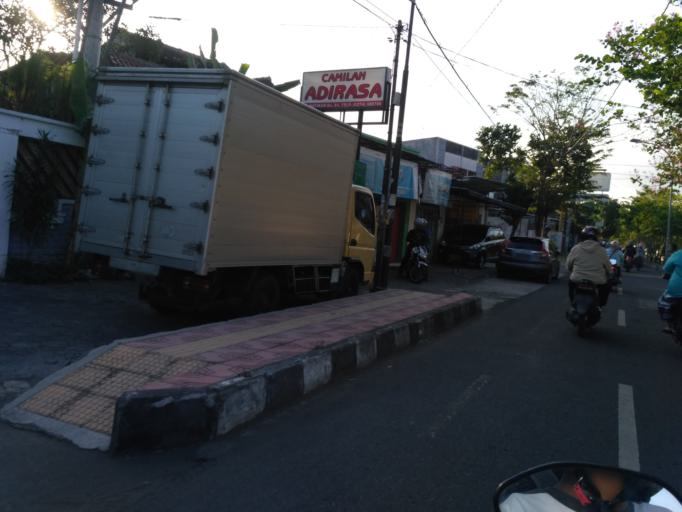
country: ID
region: Daerah Istimewa Yogyakarta
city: Yogyakarta
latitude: -7.8138
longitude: 110.3831
